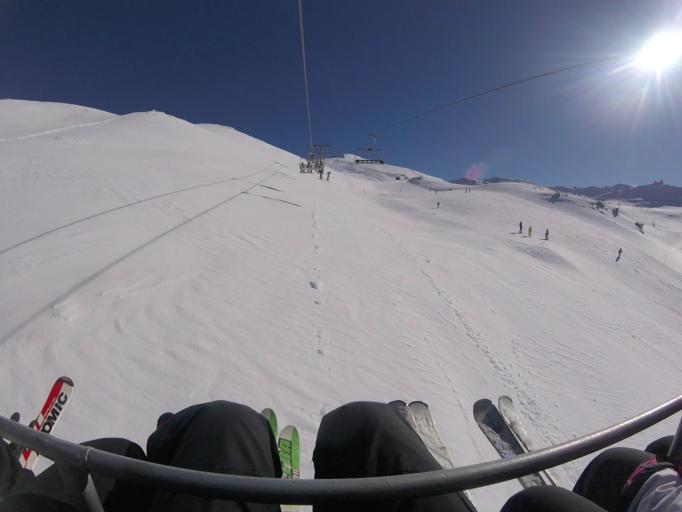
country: ES
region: Andalusia
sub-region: Provincia de Granada
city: Guejar-Sierra
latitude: 37.0719
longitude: -3.3828
